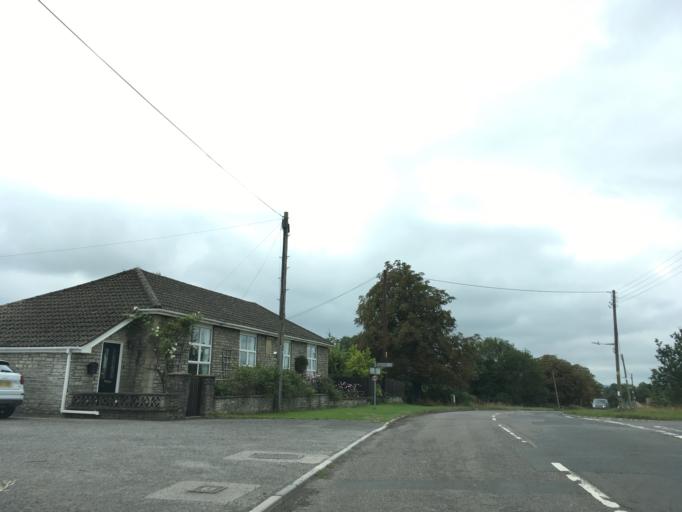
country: GB
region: England
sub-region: South Gloucestershire
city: Siston
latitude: 51.4631
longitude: -2.4597
